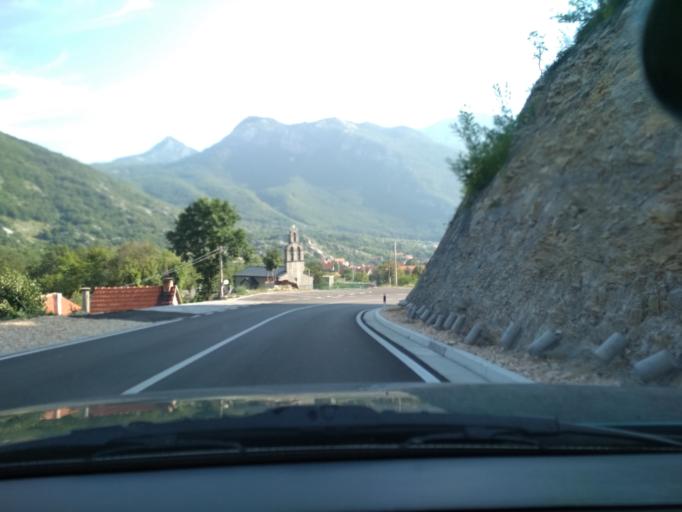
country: ME
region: Kotor
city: Kotor
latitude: 42.4372
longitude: 18.8310
